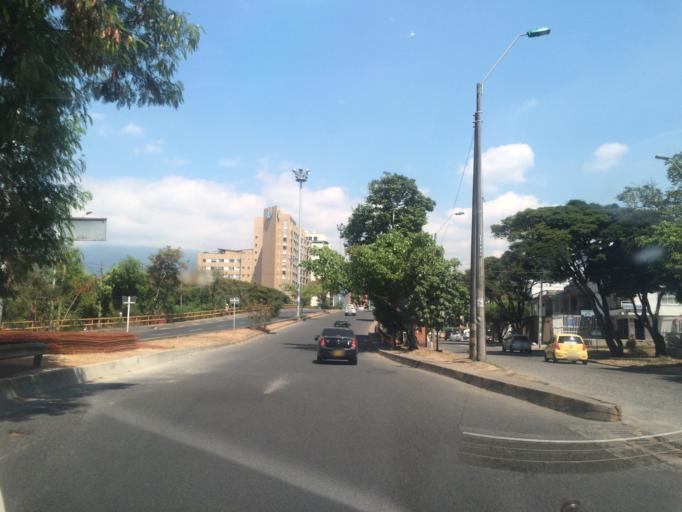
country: CO
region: Valle del Cauca
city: Cali
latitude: 3.4098
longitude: -76.5369
